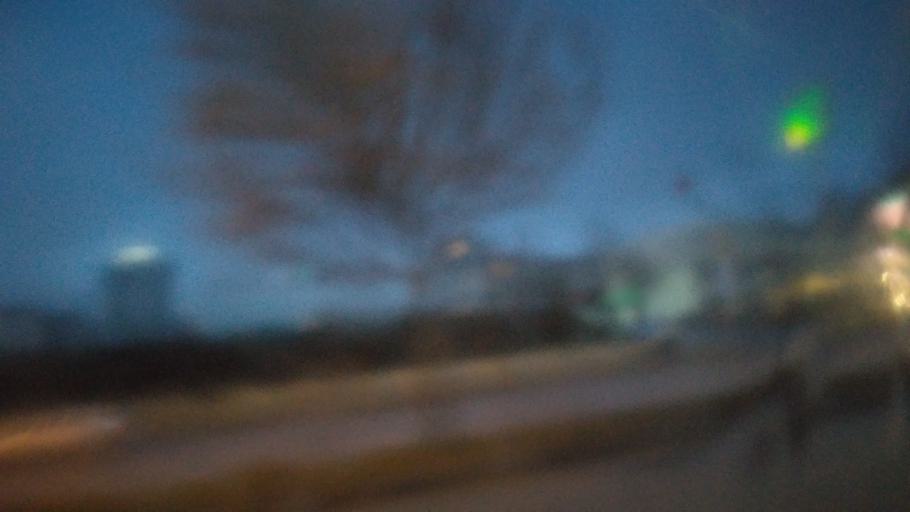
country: TR
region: Ankara
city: Ankara
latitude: 39.9688
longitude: 32.8253
